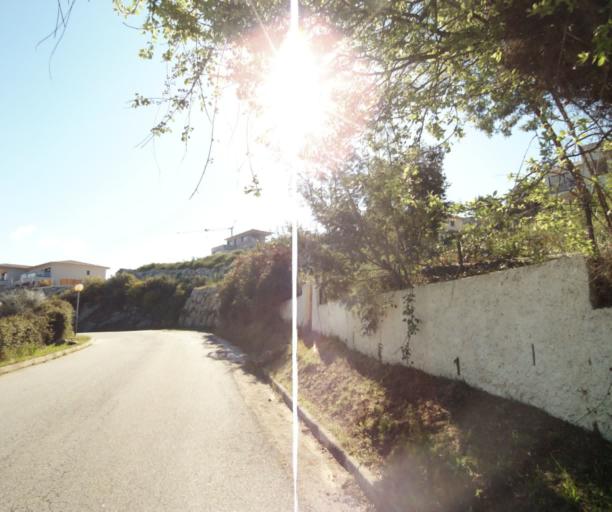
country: FR
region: Corsica
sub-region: Departement de la Corse-du-Sud
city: Propriano
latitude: 41.6691
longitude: 8.9015
